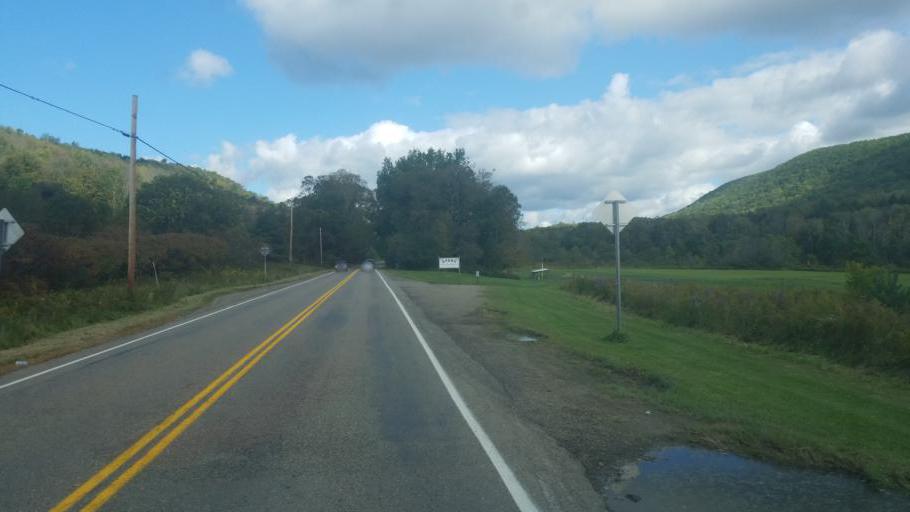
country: US
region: New York
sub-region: Allegany County
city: Cuba
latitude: 42.2195
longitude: -78.3112
